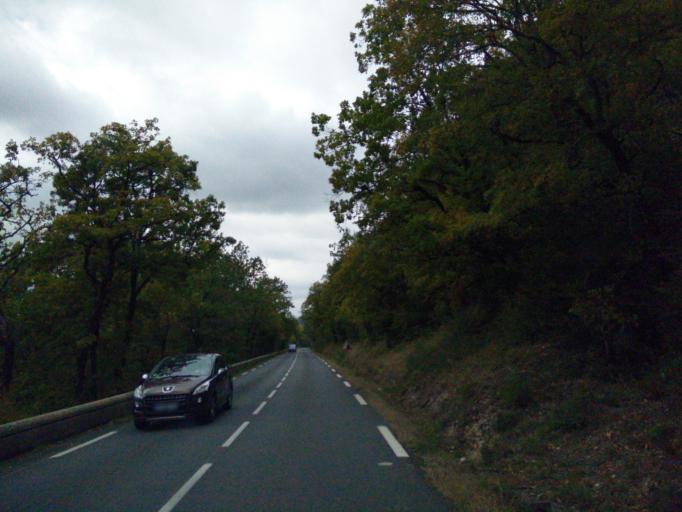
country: FR
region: Midi-Pyrenees
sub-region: Departement du Lot
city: Prayssac
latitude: 44.5109
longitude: 1.1214
